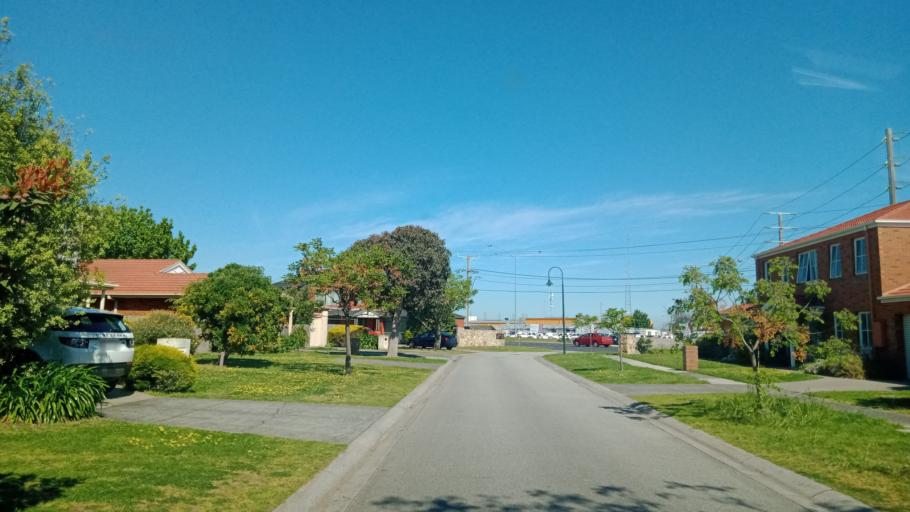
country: AU
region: Victoria
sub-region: Monash
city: Oakleigh South
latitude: -37.9372
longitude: 145.0731
